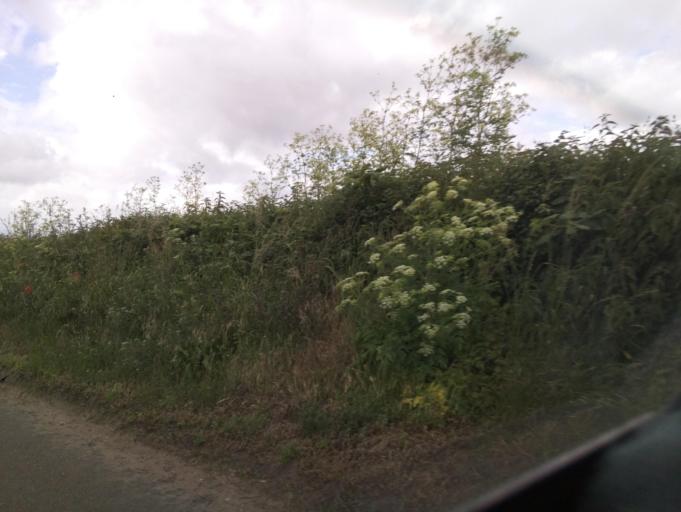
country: GB
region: England
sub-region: Dudley
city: Kingswinford
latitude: 52.4539
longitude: -2.2061
